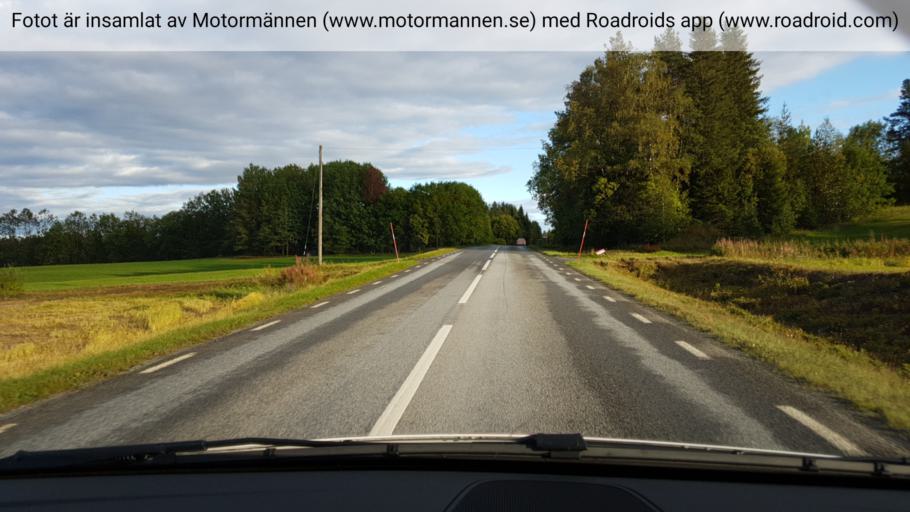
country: SE
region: Jaemtland
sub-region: Krokoms Kommun
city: Krokom
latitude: 63.1385
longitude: 14.1917
